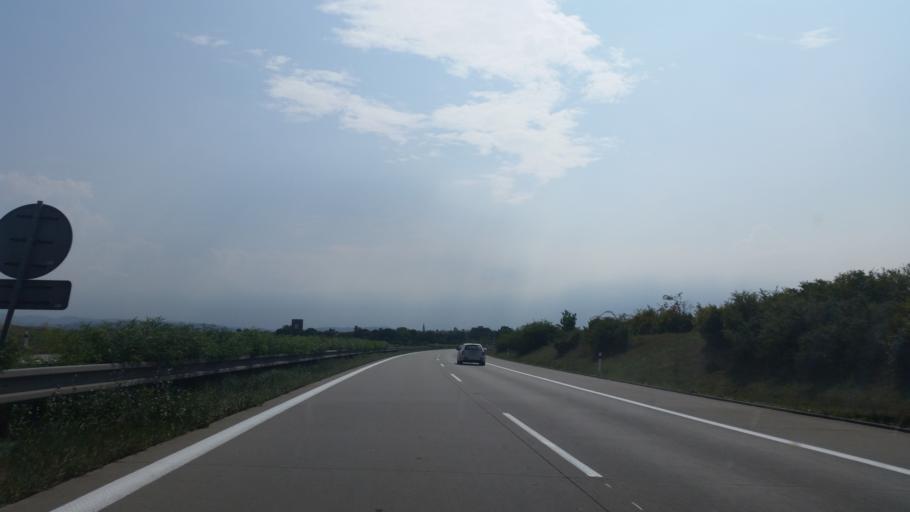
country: CZ
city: Studenka
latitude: 49.7502
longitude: 18.0940
